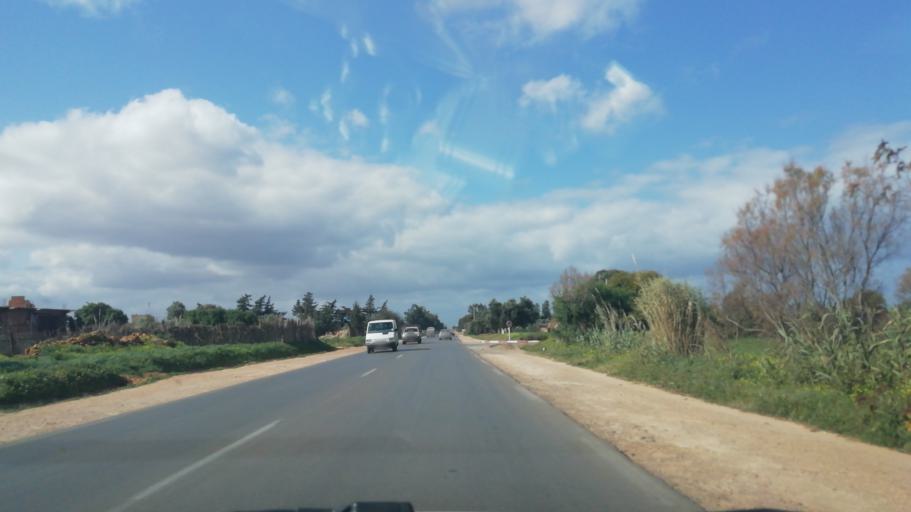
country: DZ
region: Relizane
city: Mazouna
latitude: 36.2573
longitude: 0.5919
